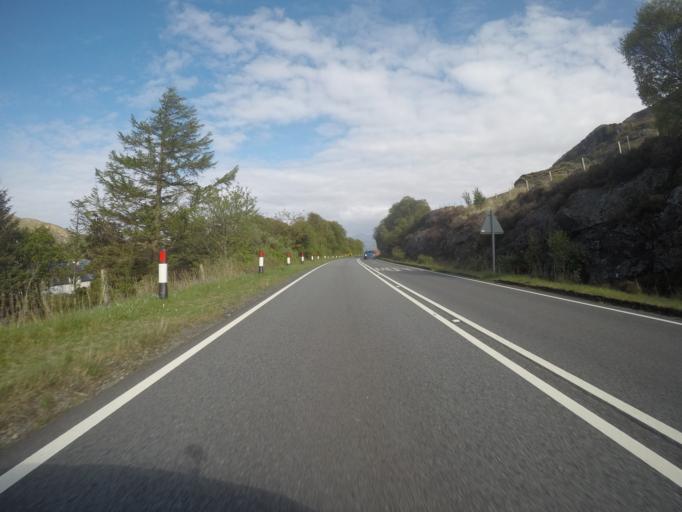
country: GB
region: Scotland
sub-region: Highland
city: Portree
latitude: 57.2688
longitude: -5.9725
